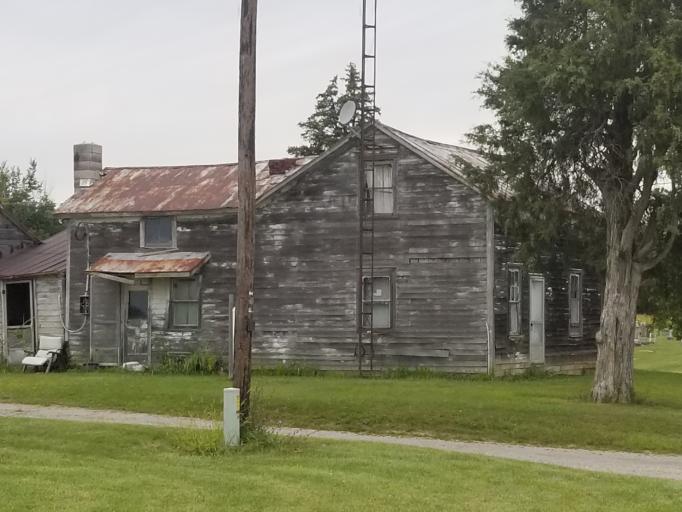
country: US
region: Ohio
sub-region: Wyandot County
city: Upper Sandusky
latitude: 40.8762
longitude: -83.1892
